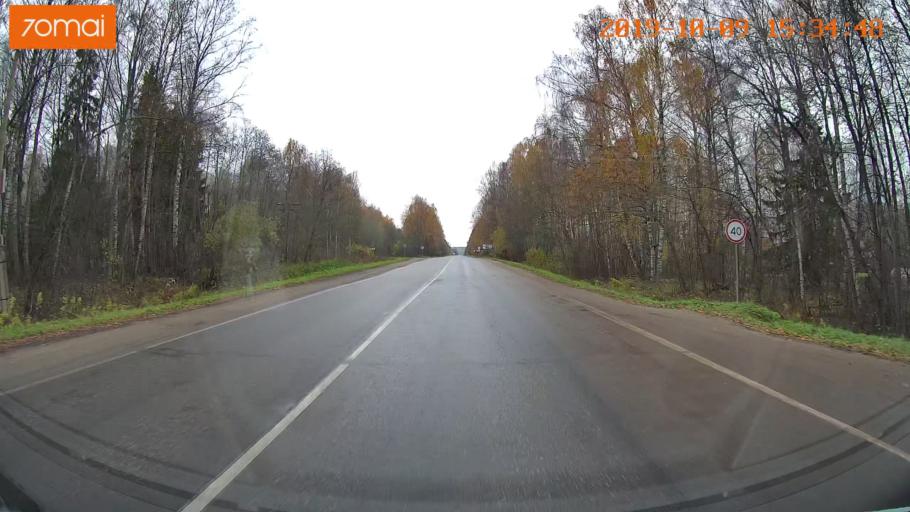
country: RU
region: Kostroma
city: Oktyabr'skiy
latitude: 57.9379
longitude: 41.2389
